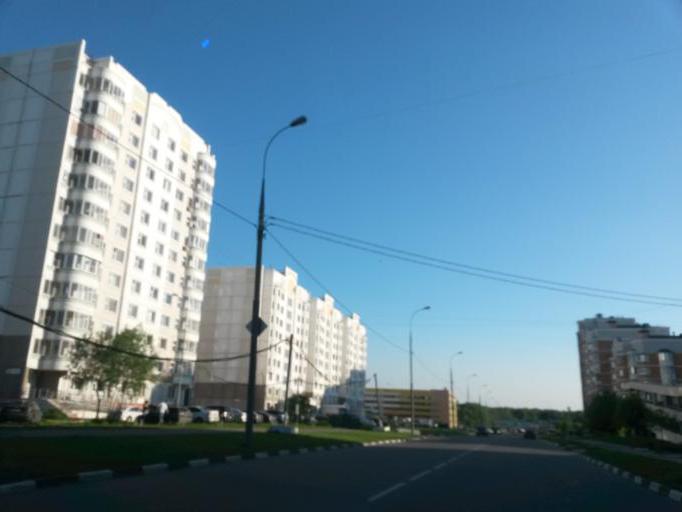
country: RU
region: Moskovskaya
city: Shcherbinka
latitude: 55.5449
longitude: 37.5623
